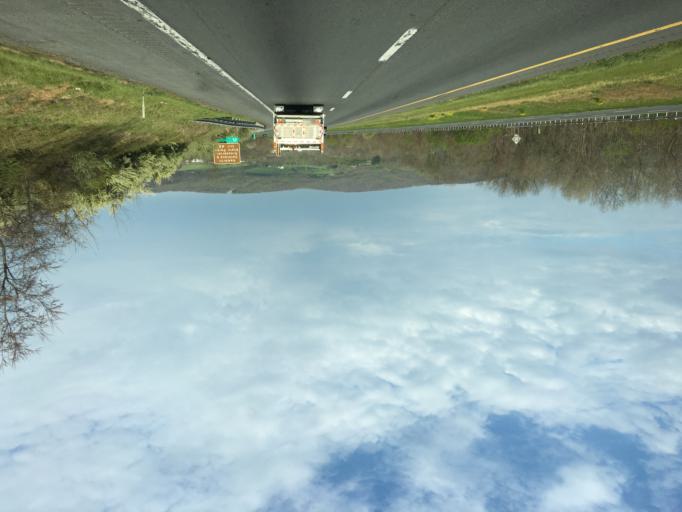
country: US
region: Maryland
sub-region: Frederick County
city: Myersville
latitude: 39.4859
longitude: -77.5516
